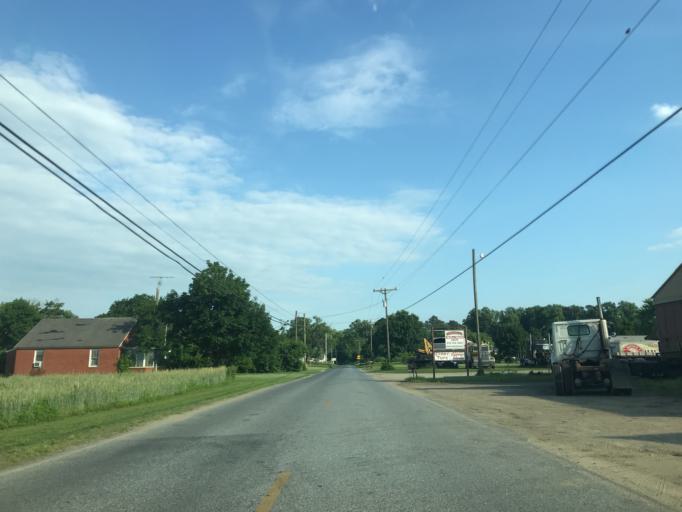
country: US
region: Maryland
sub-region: Caroline County
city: Federalsburg
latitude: 38.7151
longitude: -75.7786
